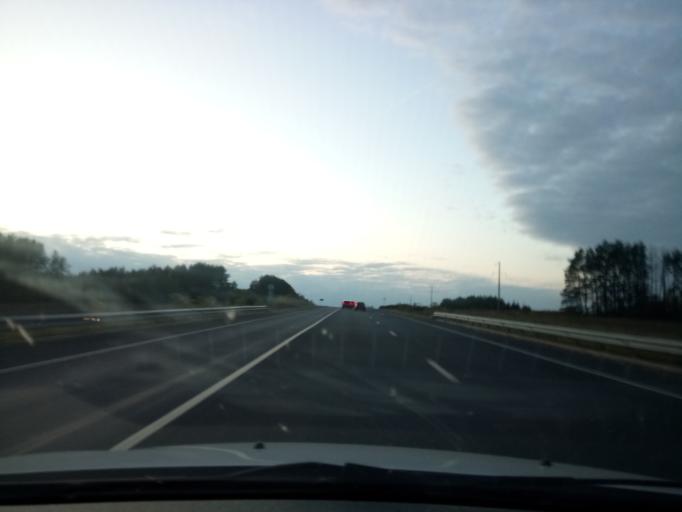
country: RU
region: Nizjnij Novgorod
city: Bol'shoye Murashkino
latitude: 55.8929
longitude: 44.7368
